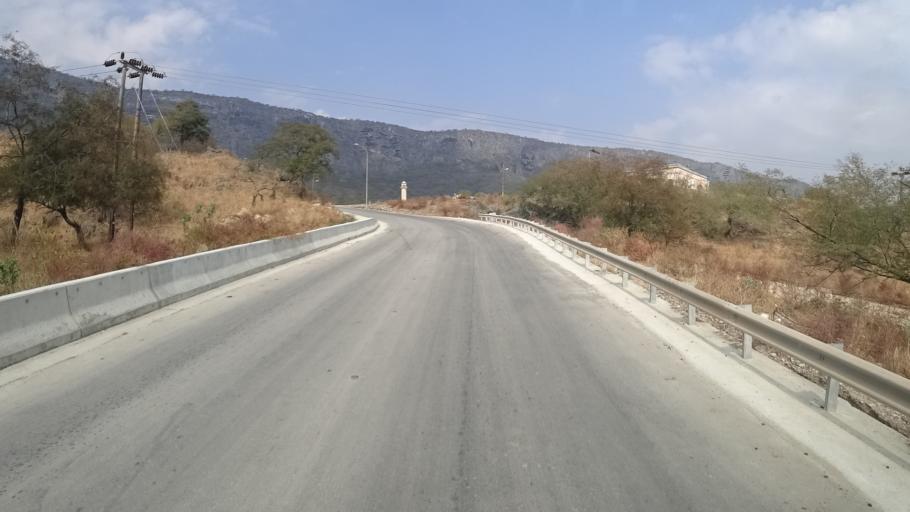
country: YE
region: Al Mahrah
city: Hawf
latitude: 16.7116
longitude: 53.2519
